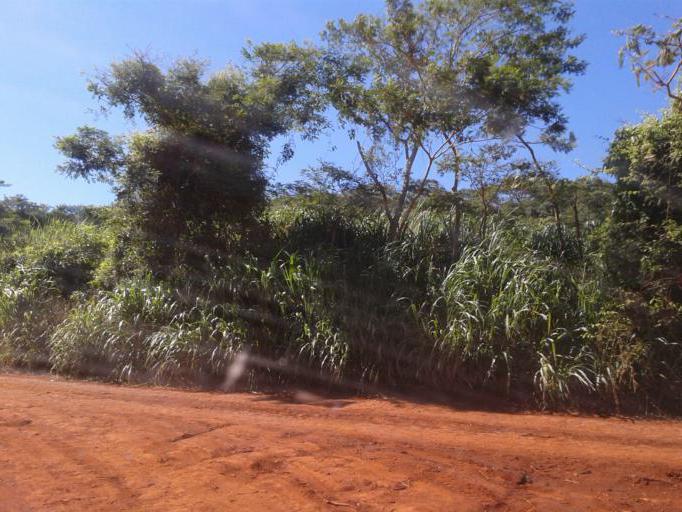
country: BR
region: Minas Gerais
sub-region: Capinopolis
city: Capinopolis
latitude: -18.6794
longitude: -49.6303
